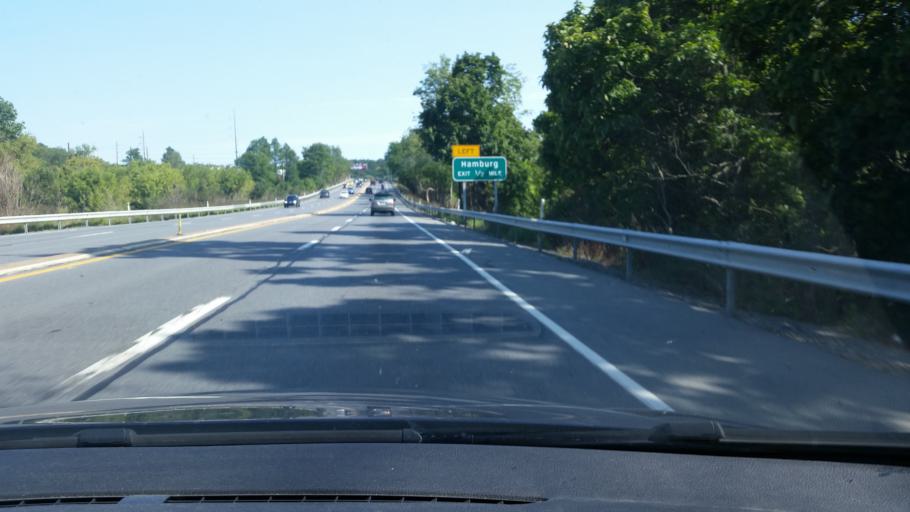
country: US
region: Pennsylvania
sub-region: Berks County
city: Hamburg
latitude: 40.5465
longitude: -75.9852
